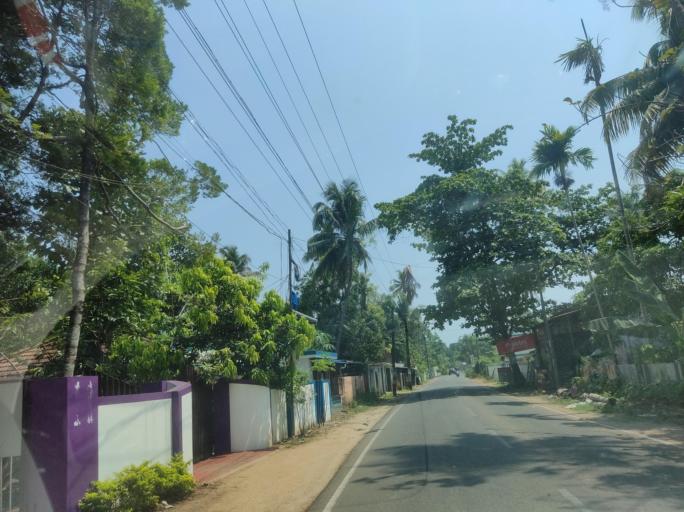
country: IN
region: Kerala
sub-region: Alappuzha
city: Kutiatodu
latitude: 9.8128
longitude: 76.3003
